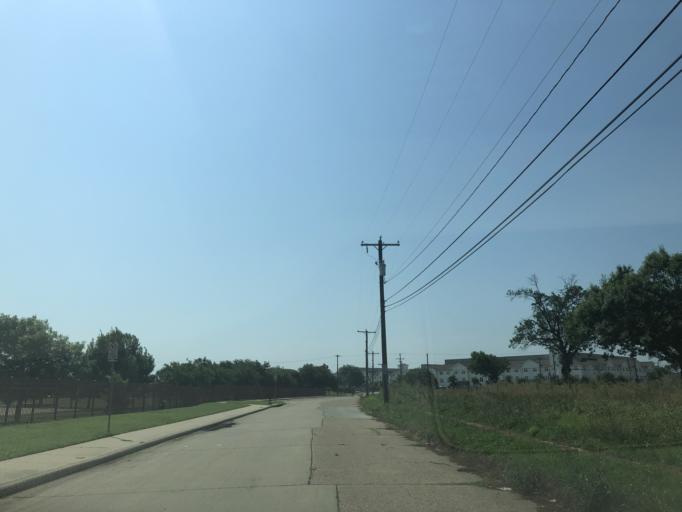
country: US
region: Texas
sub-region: Dallas County
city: Cockrell Hill
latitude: 32.7876
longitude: -96.8642
